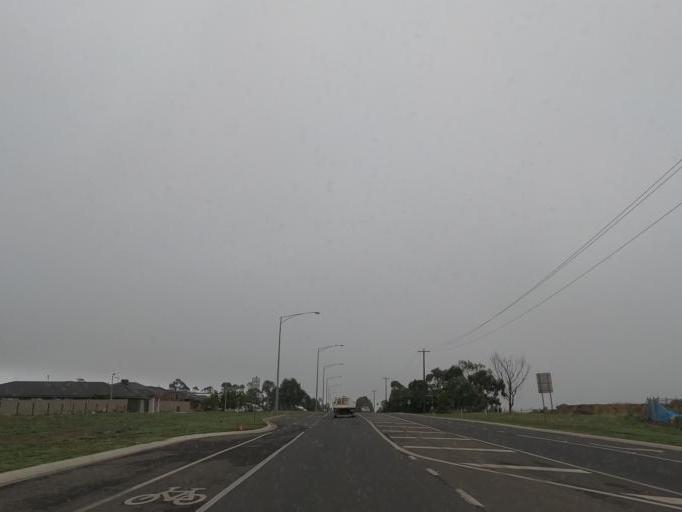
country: AU
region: Victoria
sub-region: Ballarat North
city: Newington
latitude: -37.5621
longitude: 143.8119
